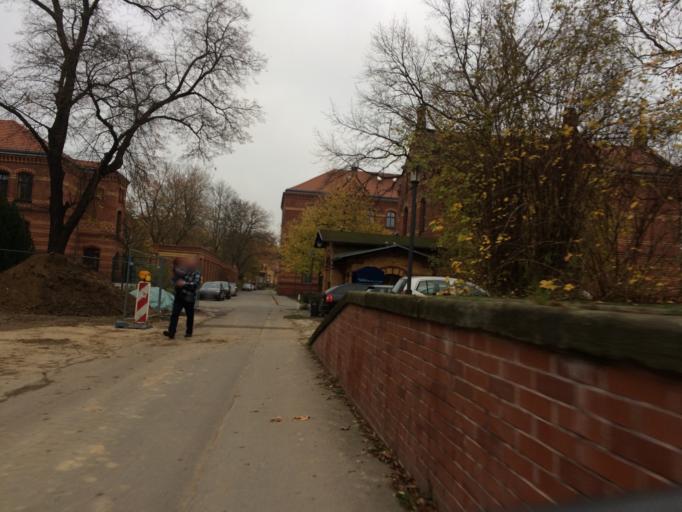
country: DE
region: Berlin
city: Lichtenberg
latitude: 52.5287
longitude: 13.5084
